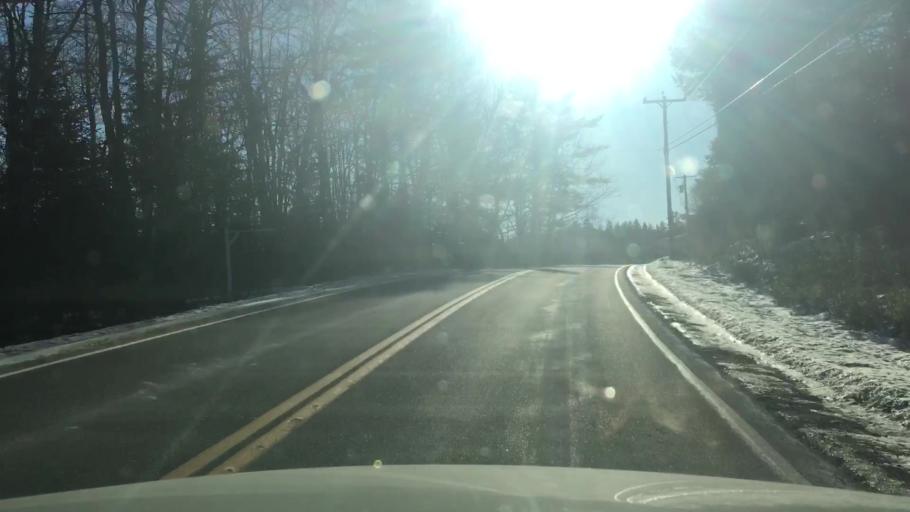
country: US
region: Maine
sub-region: Hancock County
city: Orland
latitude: 44.5214
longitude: -68.7478
